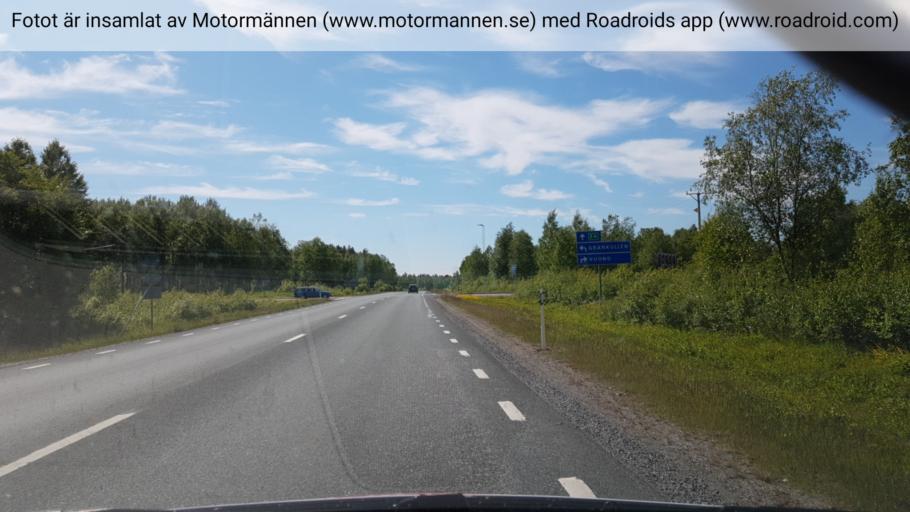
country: SE
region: Norrbotten
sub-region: Haparanda Kommun
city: Haparanda
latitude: 65.8278
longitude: 24.0781
